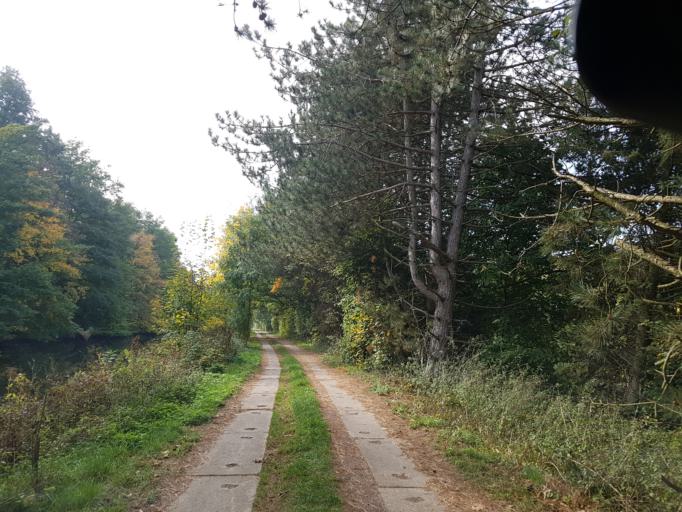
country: DE
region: Saxony
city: Waldheim
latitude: 51.0867
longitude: 13.0247
